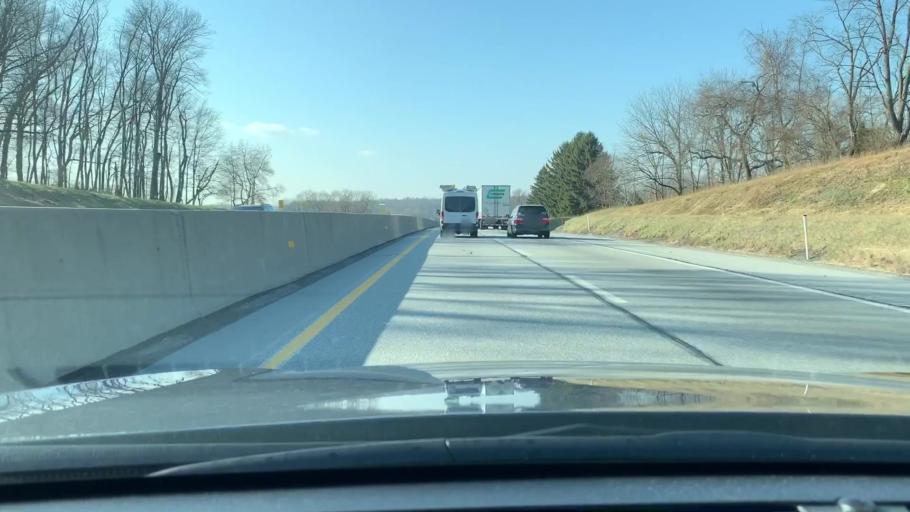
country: US
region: Pennsylvania
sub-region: Lancaster County
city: Elizabethtown
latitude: 40.2084
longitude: -76.6286
